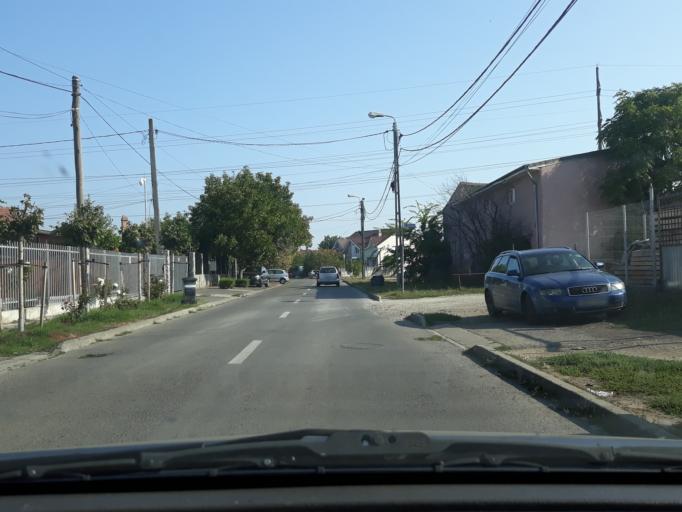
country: RO
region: Bihor
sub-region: Comuna Biharea
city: Oradea
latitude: 47.0314
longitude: 21.9376
